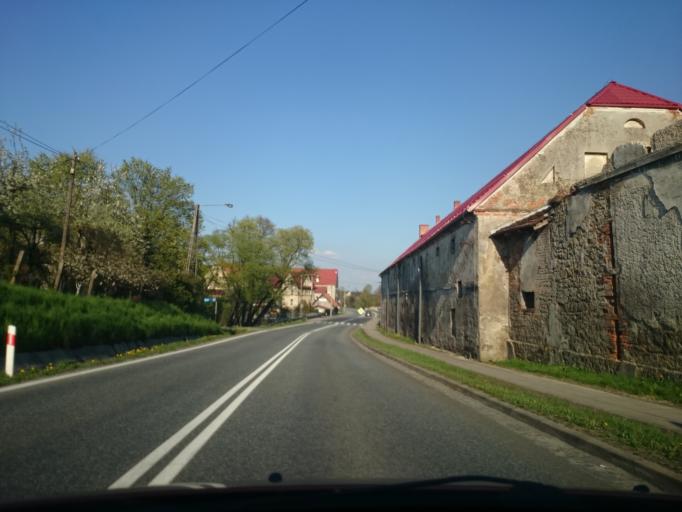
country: PL
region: Lower Silesian Voivodeship
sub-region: Powiat klodzki
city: Polanica-Zdroj
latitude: 50.4269
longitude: 16.5428
